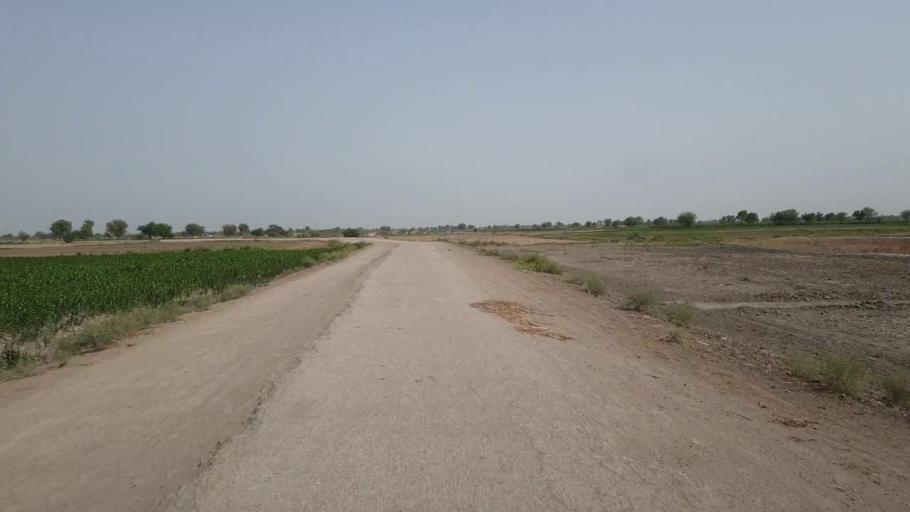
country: PK
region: Sindh
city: Daulatpur
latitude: 26.5515
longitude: 67.9919
